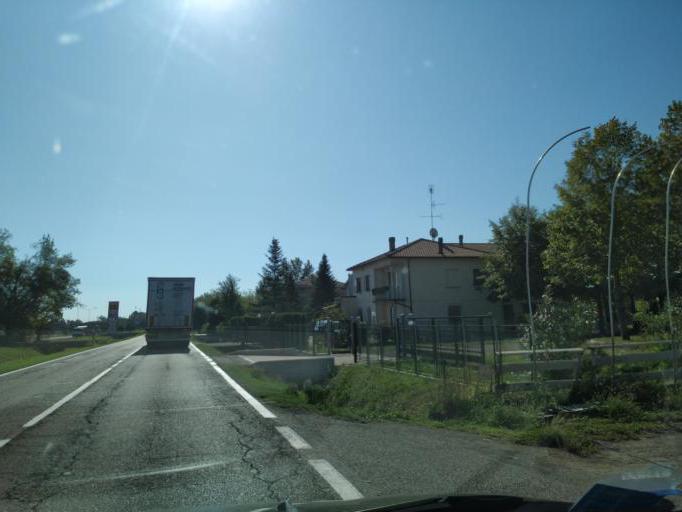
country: IT
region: Emilia-Romagna
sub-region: Provincia di Bologna
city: Sant'Agata Bolognese
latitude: 44.6566
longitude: 11.1357
